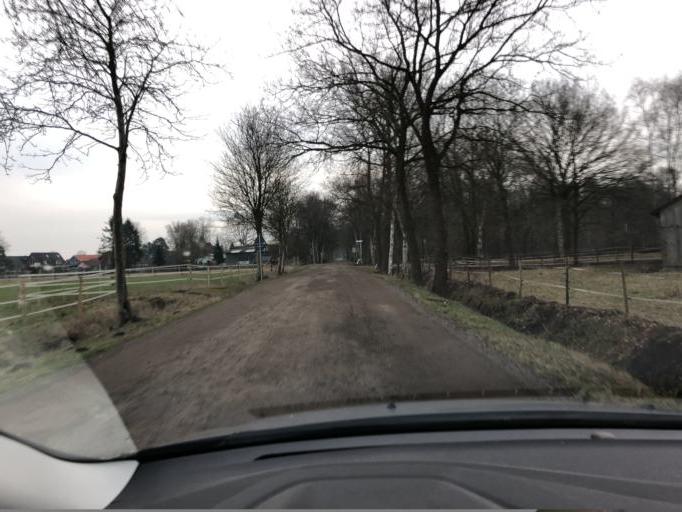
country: DE
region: Lower Saxony
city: Bad Zwischenahn
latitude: 53.1673
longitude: 8.0313
